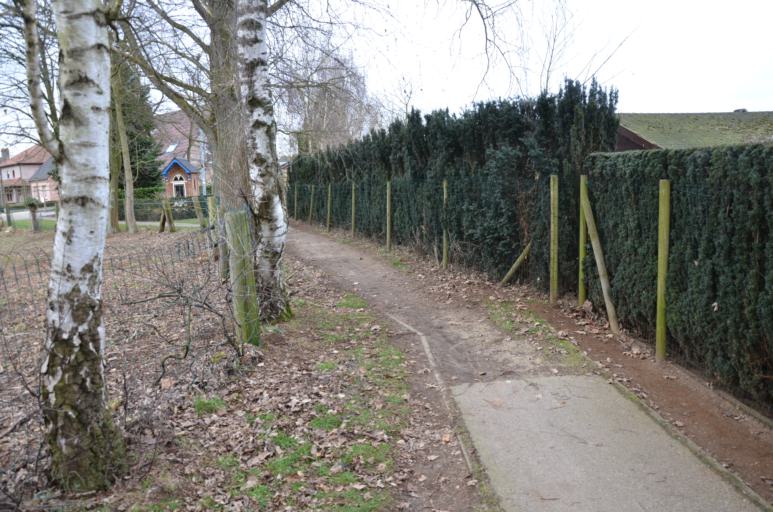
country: BE
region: Flanders
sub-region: Provincie Antwerpen
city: Lille
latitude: 51.2267
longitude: 4.8428
